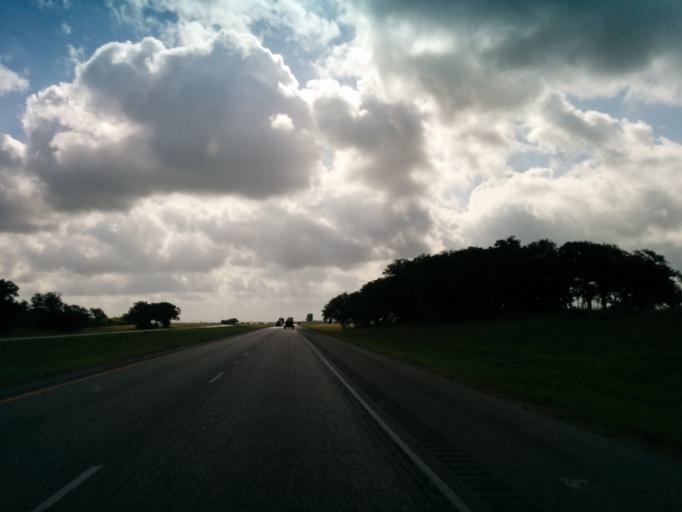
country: US
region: Texas
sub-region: Gonzales County
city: Waelder
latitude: 29.6572
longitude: -97.4249
